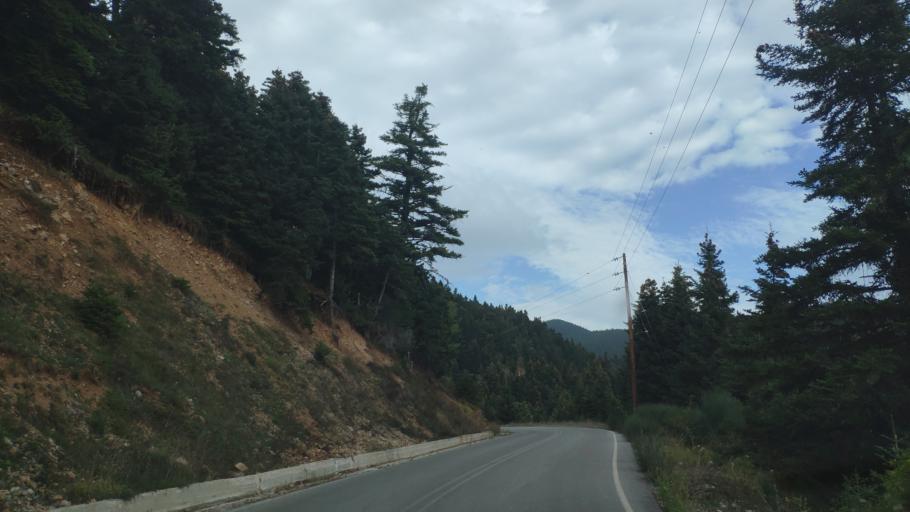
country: GR
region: Central Greece
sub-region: Nomos Fokidos
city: Amfissa
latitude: 38.6946
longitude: 22.3188
